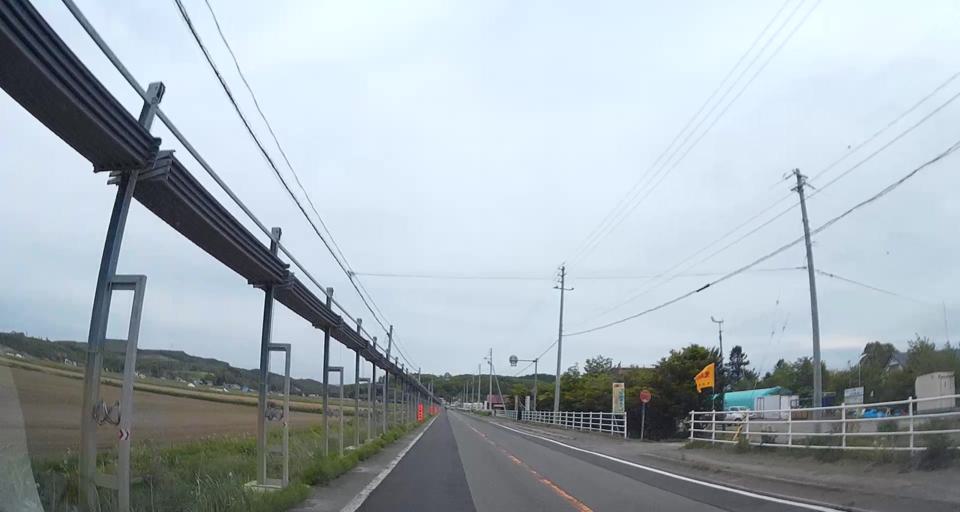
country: JP
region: Hokkaido
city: Chitose
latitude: 42.7318
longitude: 141.8870
